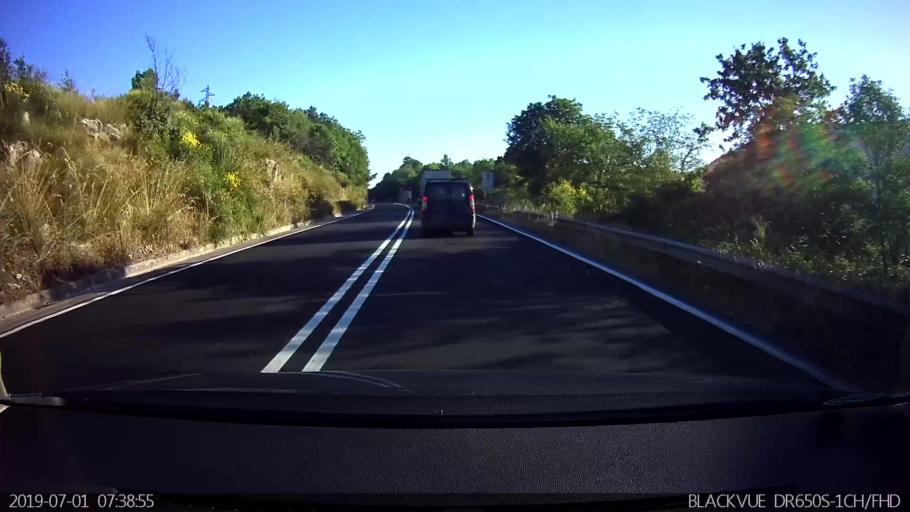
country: IT
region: Latium
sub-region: Provincia di Frosinone
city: Giuliano di Roma
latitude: 41.5462
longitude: 13.2695
